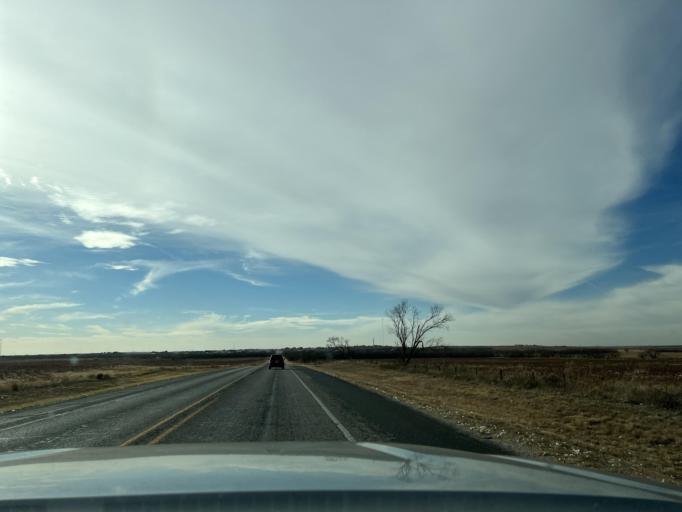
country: US
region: Texas
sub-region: Fisher County
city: Roby
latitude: 32.7502
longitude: -100.3522
